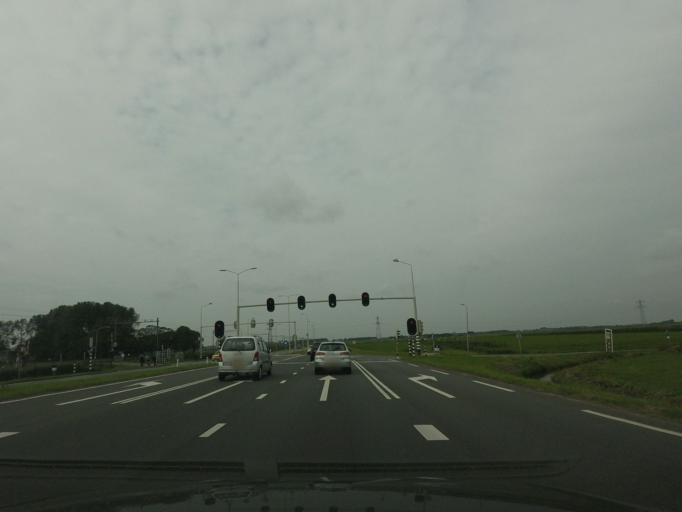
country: NL
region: North Holland
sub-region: Gemeente Uitgeest
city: Uitgeest
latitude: 52.5022
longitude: 4.7399
